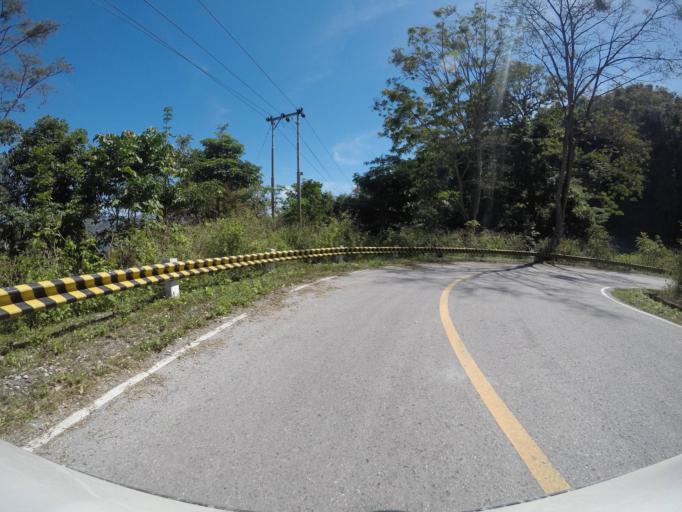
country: TL
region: Manufahi
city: Same
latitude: -8.9031
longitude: 125.9768
